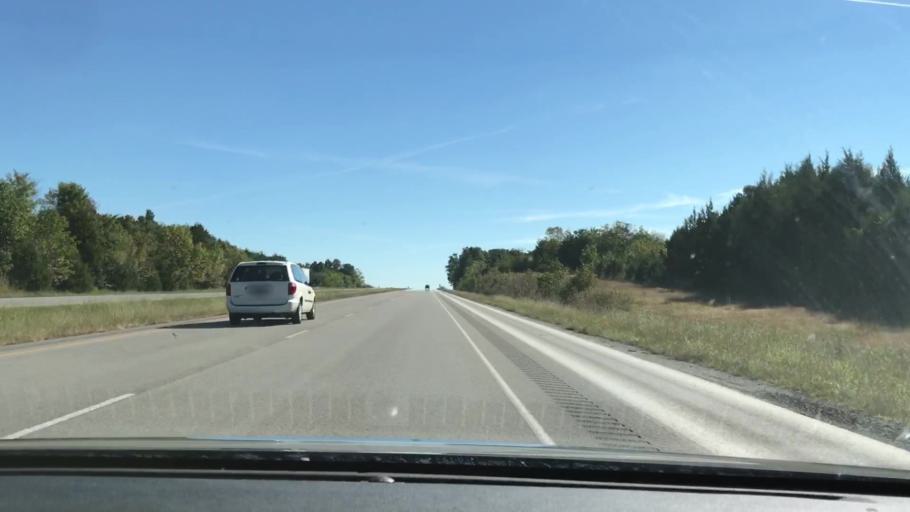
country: US
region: Kentucky
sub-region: Todd County
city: Elkton
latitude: 36.8474
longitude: -87.3179
